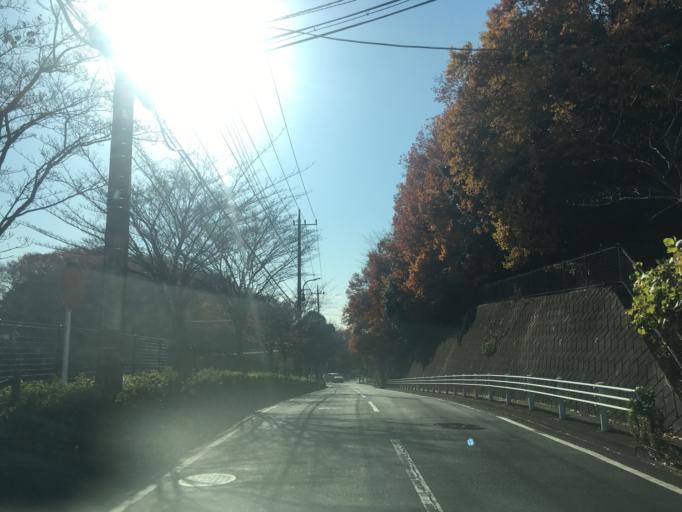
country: JP
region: Tokyo
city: Hino
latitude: 35.6125
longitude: 139.4083
